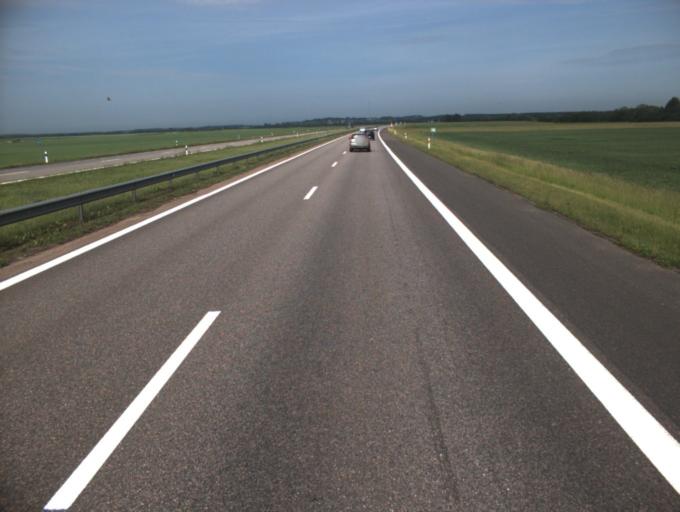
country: LT
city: Raseiniai
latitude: 55.3239
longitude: 23.1713
